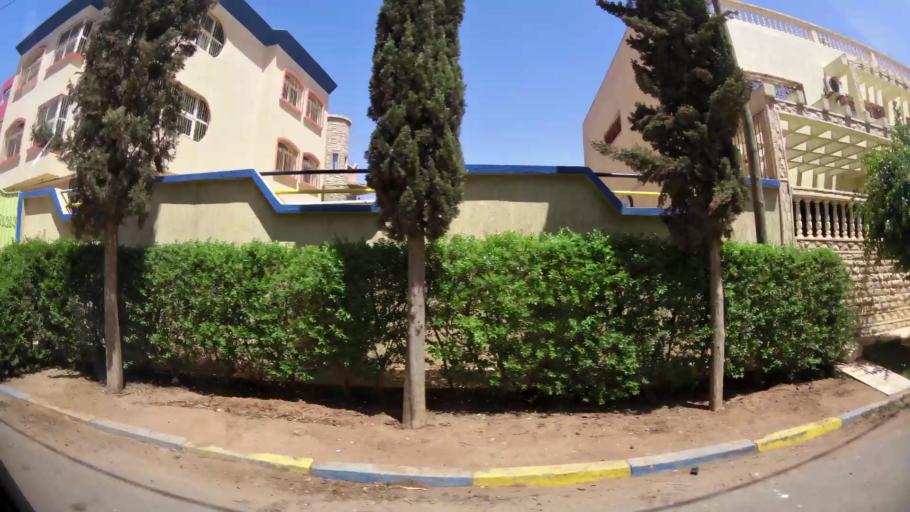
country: MA
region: Souss-Massa-Draa
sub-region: Inezgane-Ait Mellou
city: Inezgane
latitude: 30.3452
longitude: -9.4824
